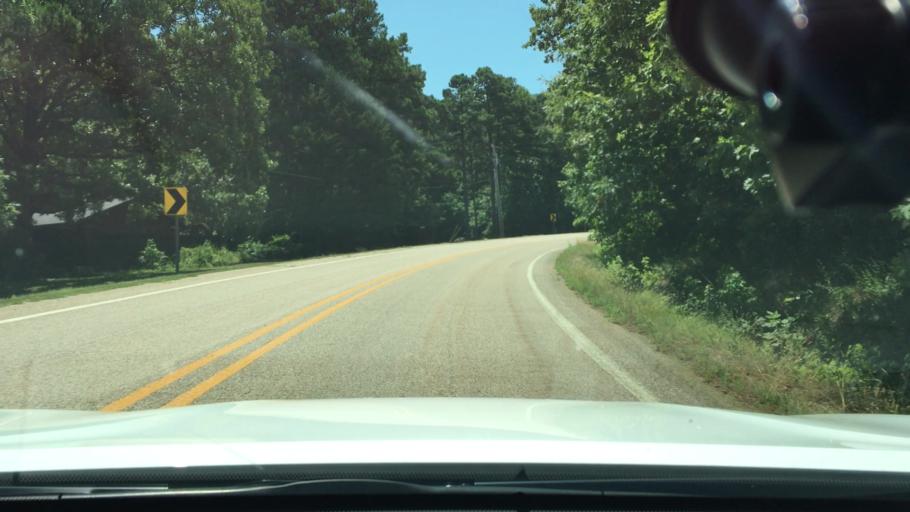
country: US
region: Arkansas
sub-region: Logan County
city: Paris
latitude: 35.1900
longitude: -93.6225
